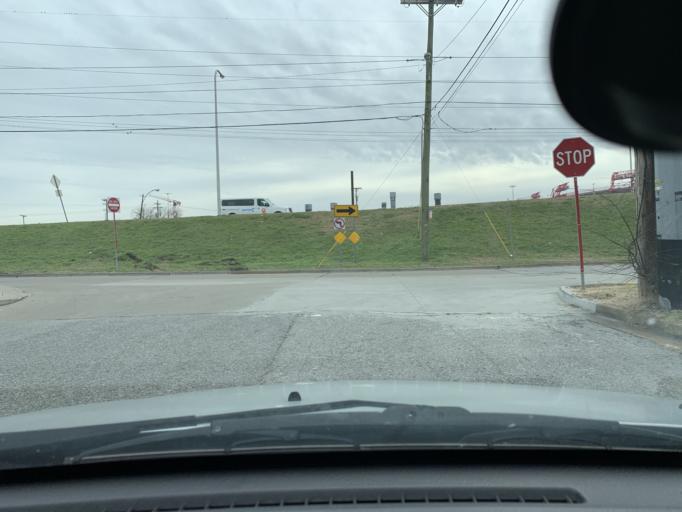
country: US
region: Tennessee
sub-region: Davidson County
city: Nashville
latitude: 36.1714
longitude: -86.7706
